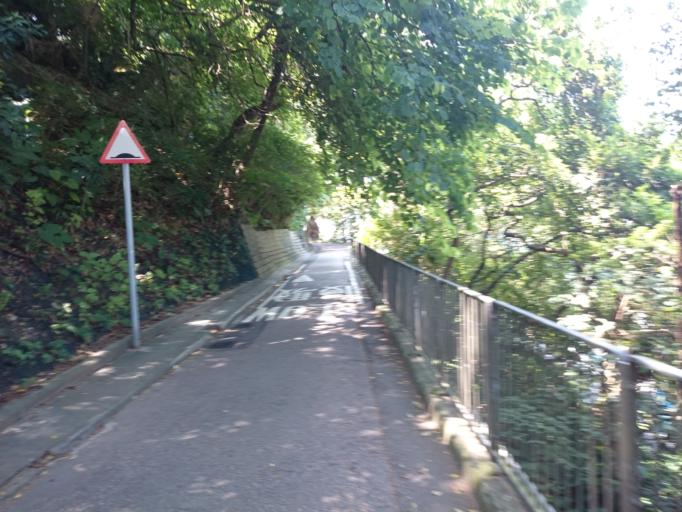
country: HK
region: Central and Western
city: Central
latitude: 22.2750
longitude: 114.1633
